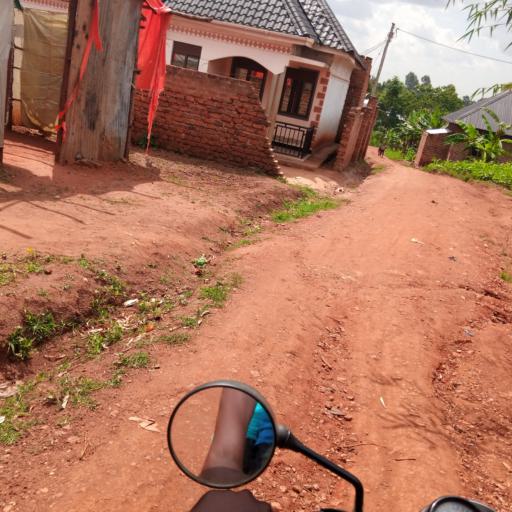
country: UG
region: Eastern Region
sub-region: Mbale District
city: Mbale
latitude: 1.1046
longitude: 34.1822
